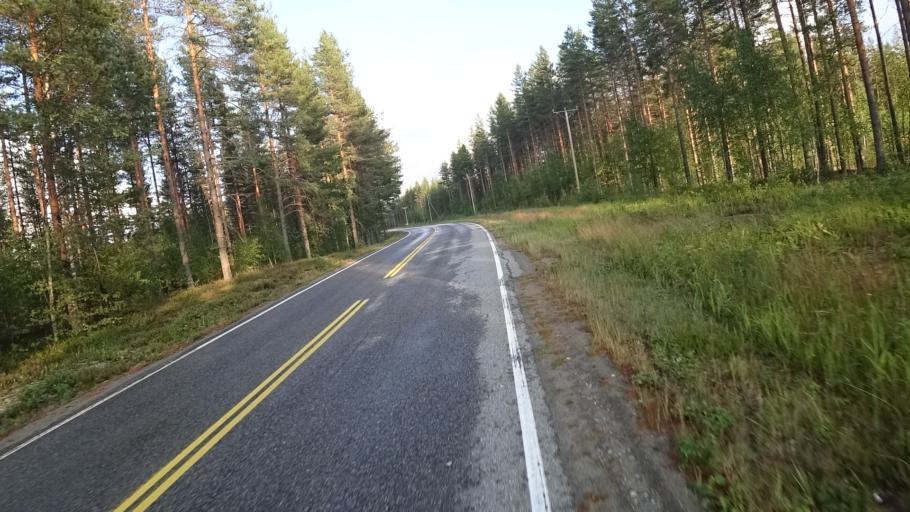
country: FI
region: North Karelia
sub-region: Joensuu
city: Ilomantsi
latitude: 62.6282
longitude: 31.0962
